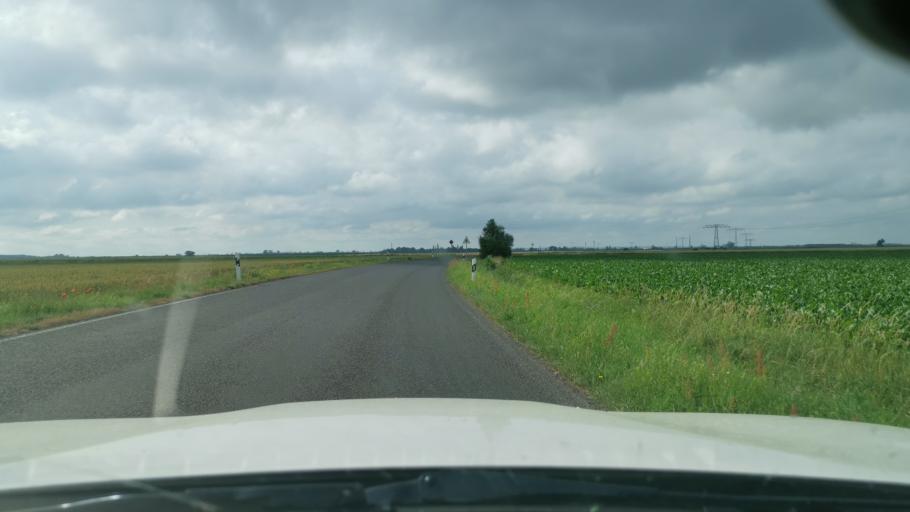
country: DE
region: Saxony
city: Torgau
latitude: 51.6323
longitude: 13.0059
